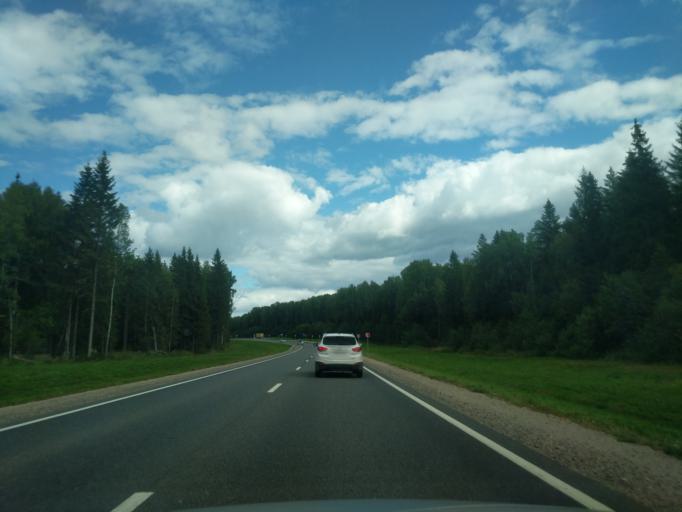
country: RU
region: Kostroma
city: Oktyabr'skiy
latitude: 57.7908
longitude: 41.1515
